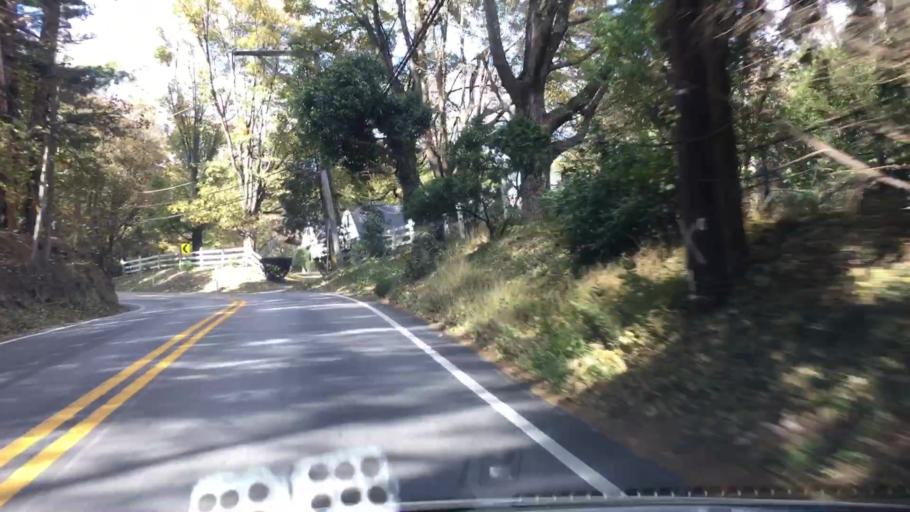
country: US
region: Pennsylvania
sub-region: Delaware County
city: Media
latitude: 39.9451
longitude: -75.3991
